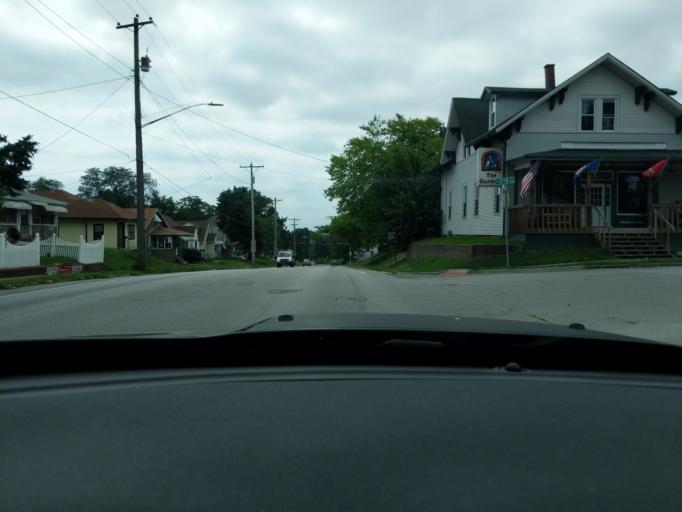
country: US
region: Iowa
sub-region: Scott County
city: Davenport
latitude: 41.5328
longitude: -90.5915
